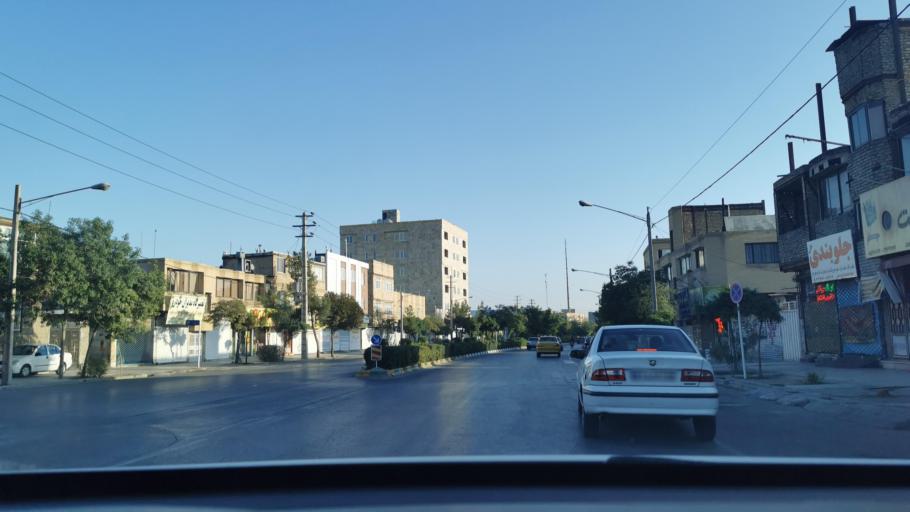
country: IR
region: Razavi Khorasan
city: Mashhad
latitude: 36.3548
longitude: 59.5131
